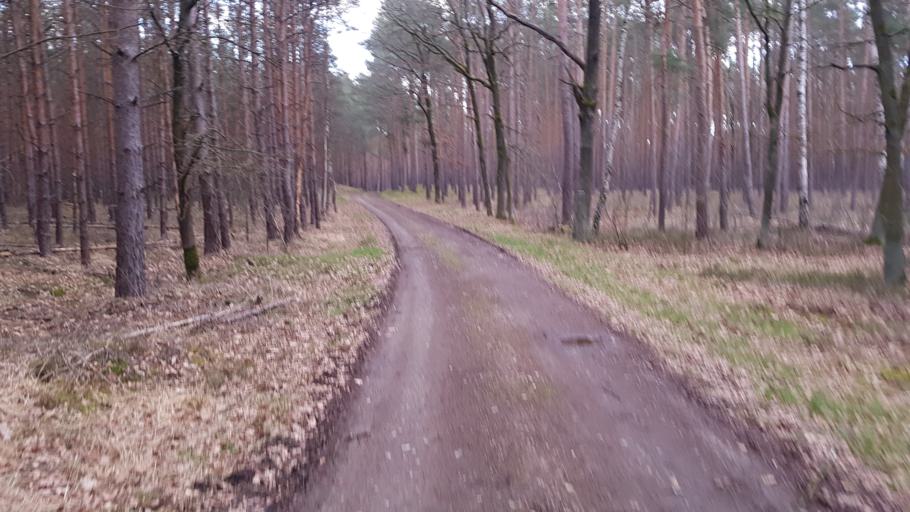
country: DE
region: Brandenburg
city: Schilda
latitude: 51.5805
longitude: 13.3190
